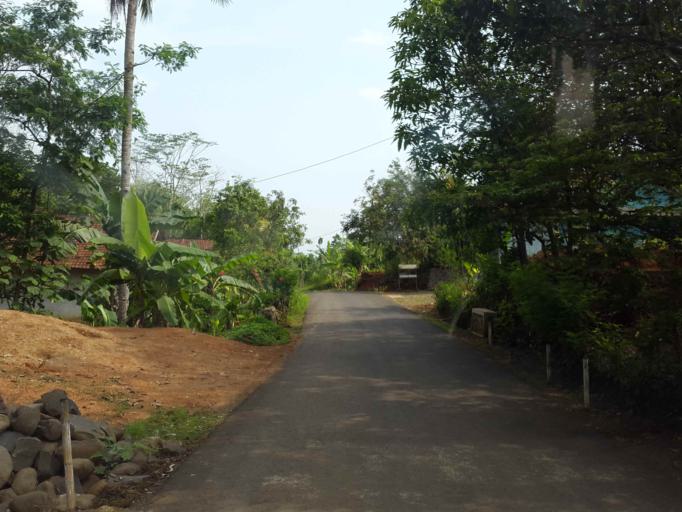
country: ID
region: Central Java
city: Sogati
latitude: -7.3200
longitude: 108.6738
